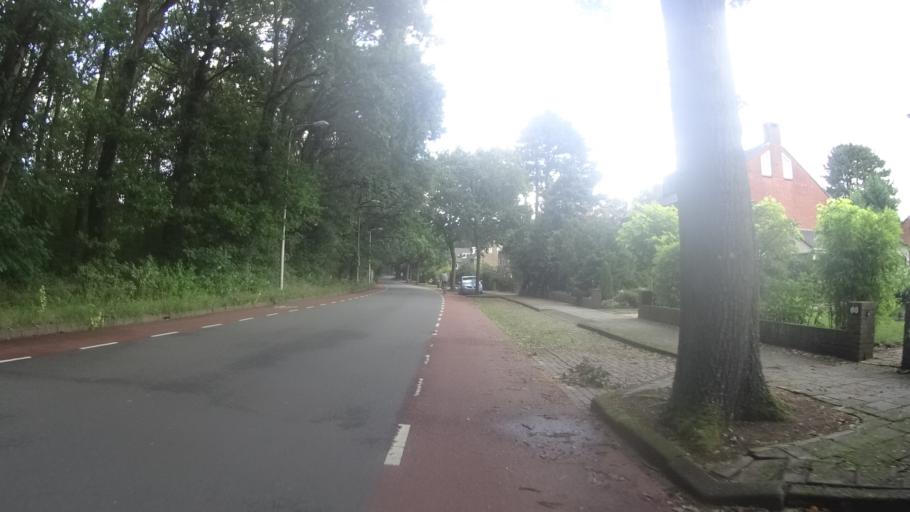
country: NL
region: North Holland
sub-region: Gemeente Bloemendaal
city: Bloemendaal
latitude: 52.4238
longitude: 4.6320
